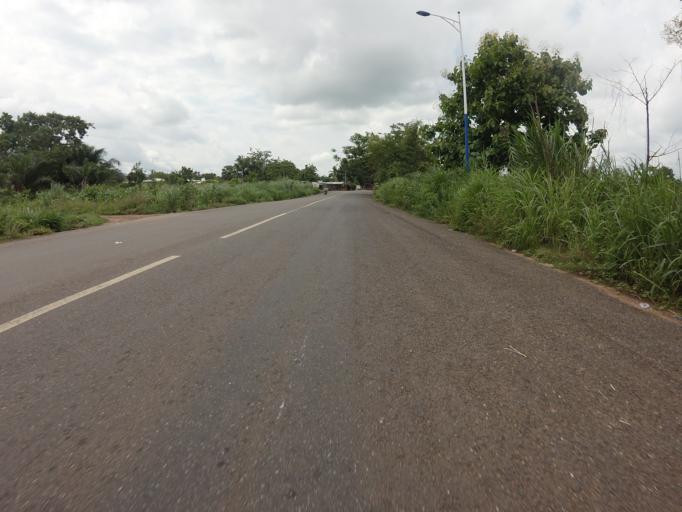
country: GH
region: Volta
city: Ho
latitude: 6.6201
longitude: 0.4952
